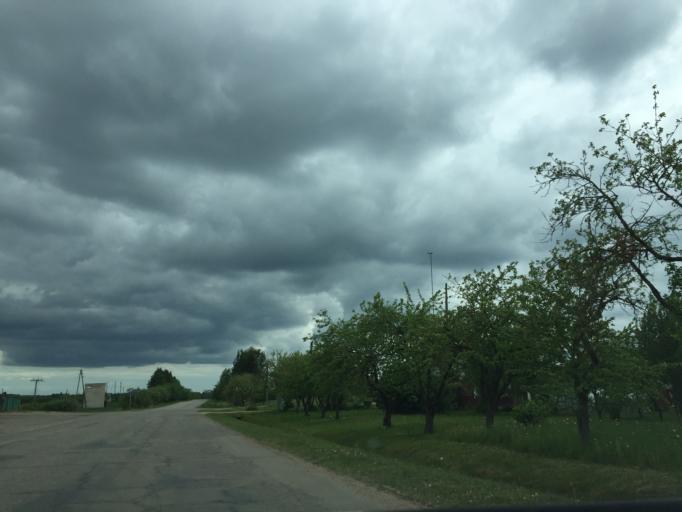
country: LV
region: Dagda
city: Dagda
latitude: 56.0988
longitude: 27.5195
